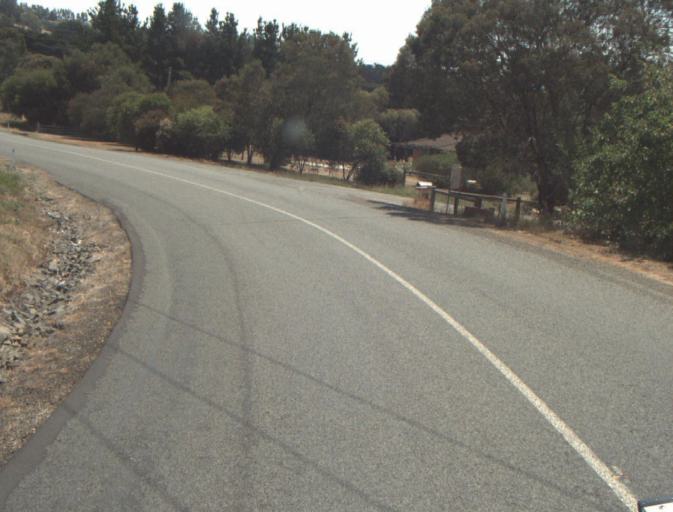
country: AU
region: Tasmania
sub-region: Launceston
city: Newstead
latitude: -41.4934
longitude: 147.2092
